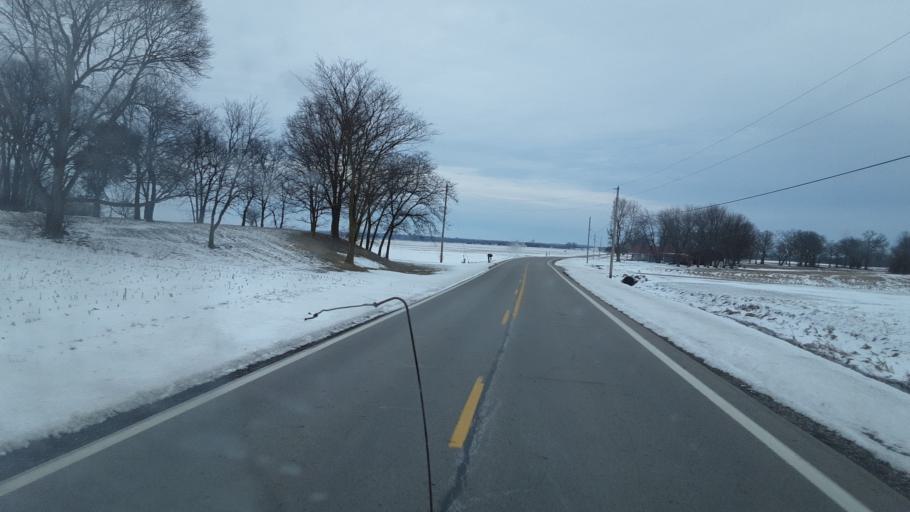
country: US
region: Ohio
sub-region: Pickaway County
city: Circleville
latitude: 39.6212
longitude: -83.0219
